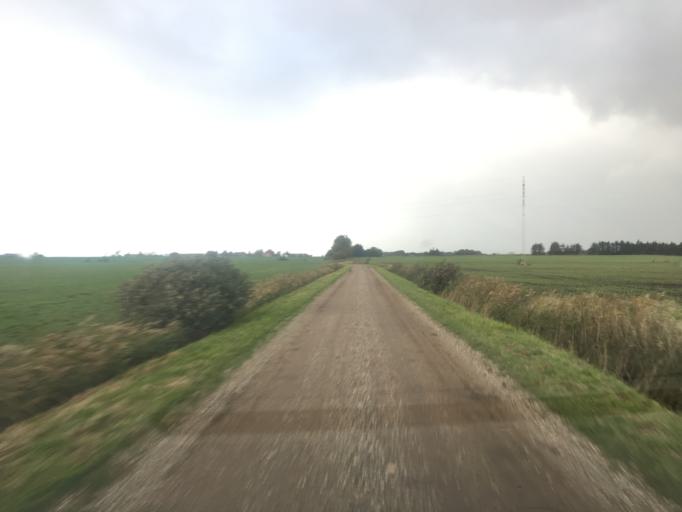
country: DE
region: Schleswig-Holstein
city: Aventoft
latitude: 54.9390
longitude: 8.7784
